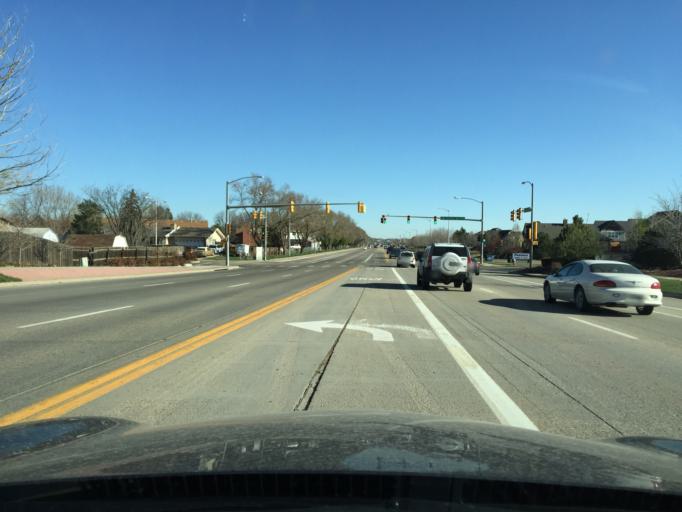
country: US
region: Colorado
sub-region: Boulder County
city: Longmont
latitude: 40.1404
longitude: -105.1025
